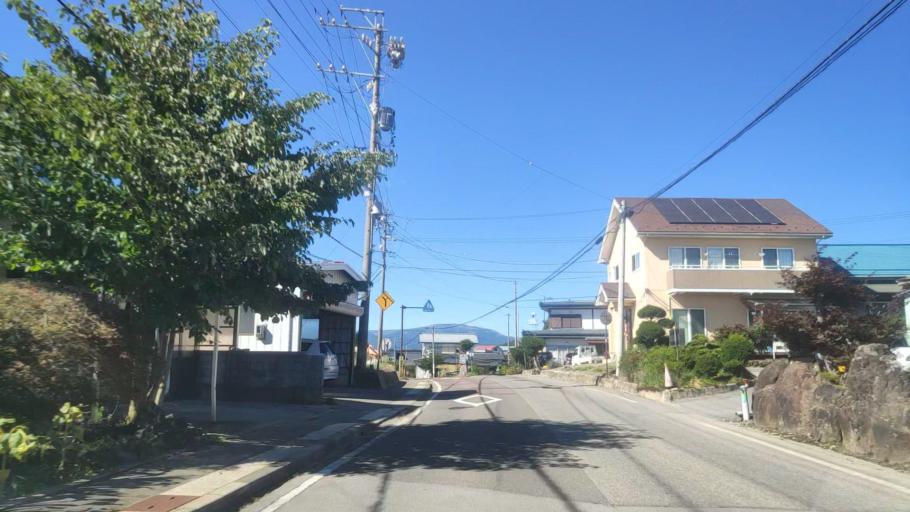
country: JP
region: Nagano
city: Chino
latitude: 35.9757
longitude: 138.2195
